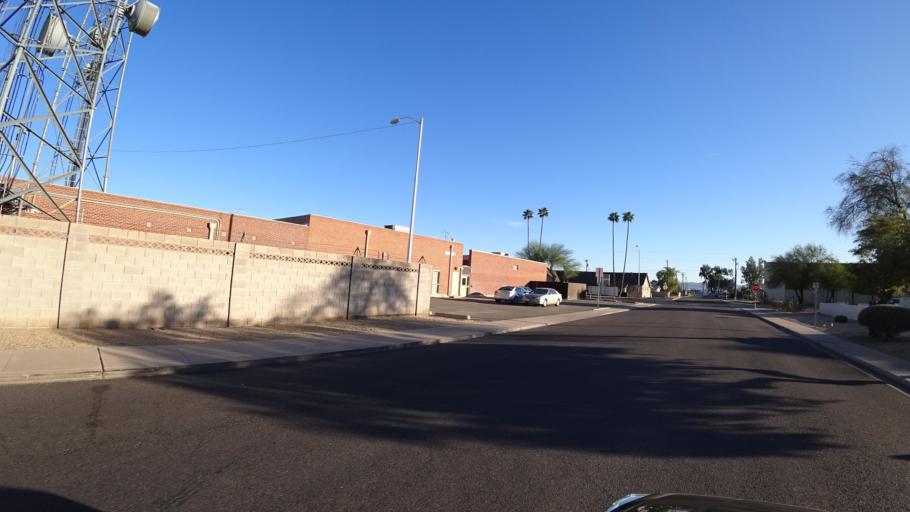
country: US
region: Arizona
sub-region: Maricopa County
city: Phoenix
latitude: 33.4739
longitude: -112.1043
